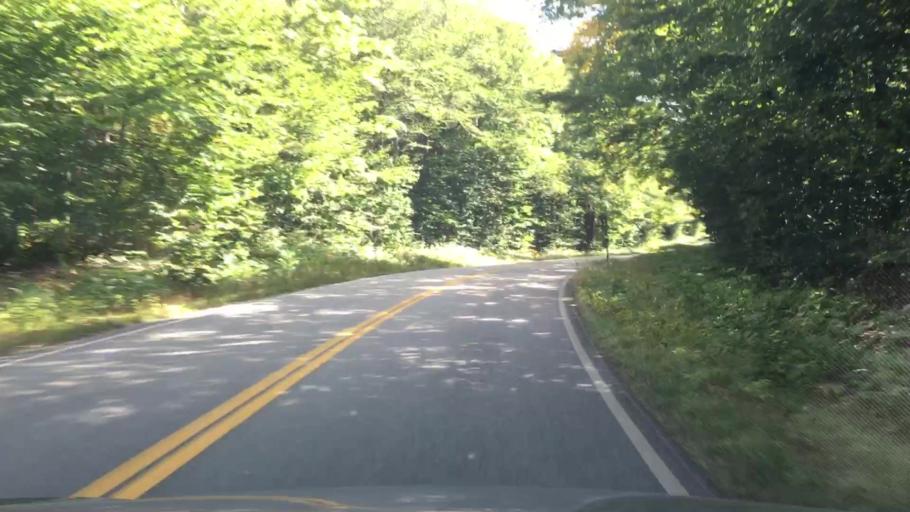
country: US
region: New Hampshire
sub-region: Carroll County
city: Tamworth
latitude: 44.0173
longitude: -71.3197
